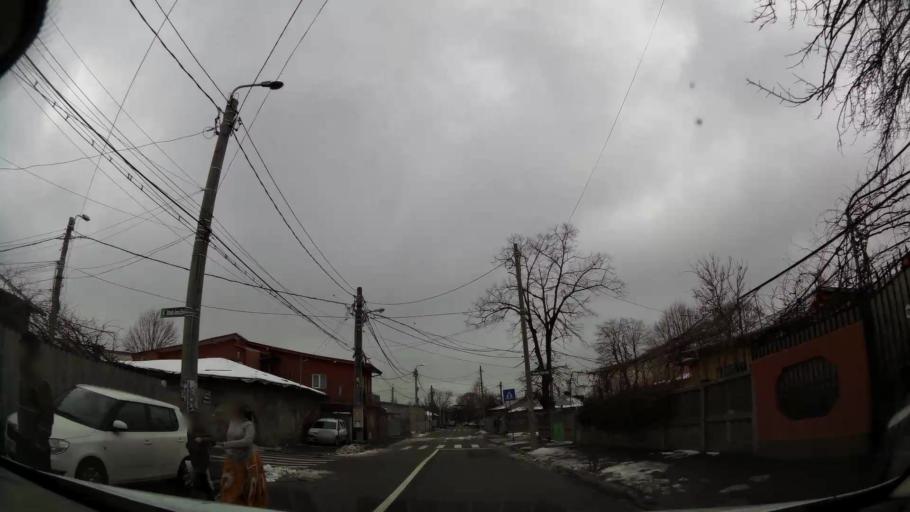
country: RO
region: Ilfov
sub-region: Comuna Chiajna
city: Rosu
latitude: 44.4804
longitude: 26.0256
